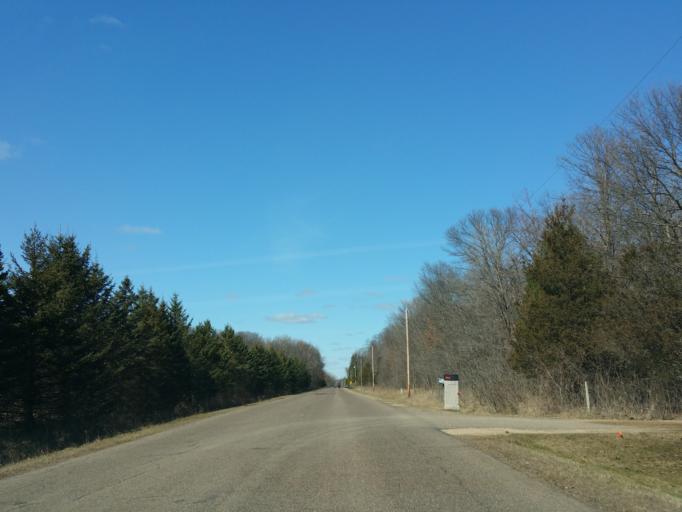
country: US
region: Minnesota
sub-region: Washington County
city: Stillwater
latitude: 45.0754
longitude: -92.7713
